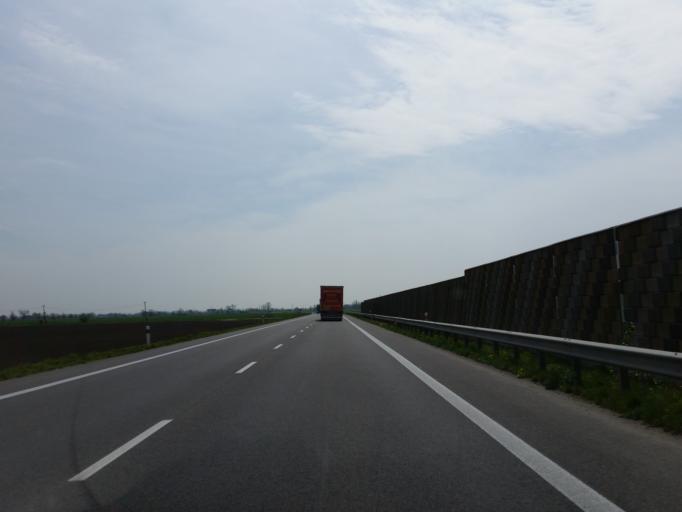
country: SK
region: Trnavsky
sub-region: Okres Galanta
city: Galanta
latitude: 48.2189
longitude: 17.7353
